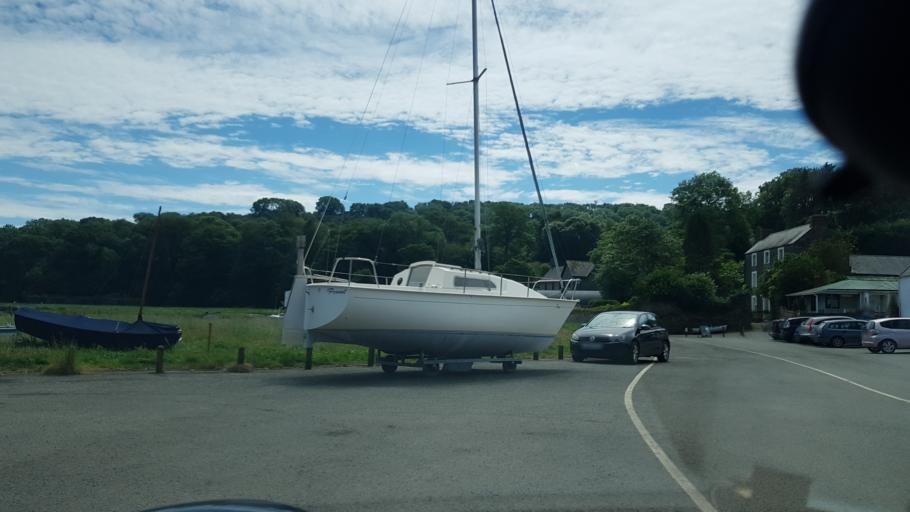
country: GB
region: Wales
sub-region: Carmarthenshire
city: Saint Clears
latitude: 51.7685
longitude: -4.4626
